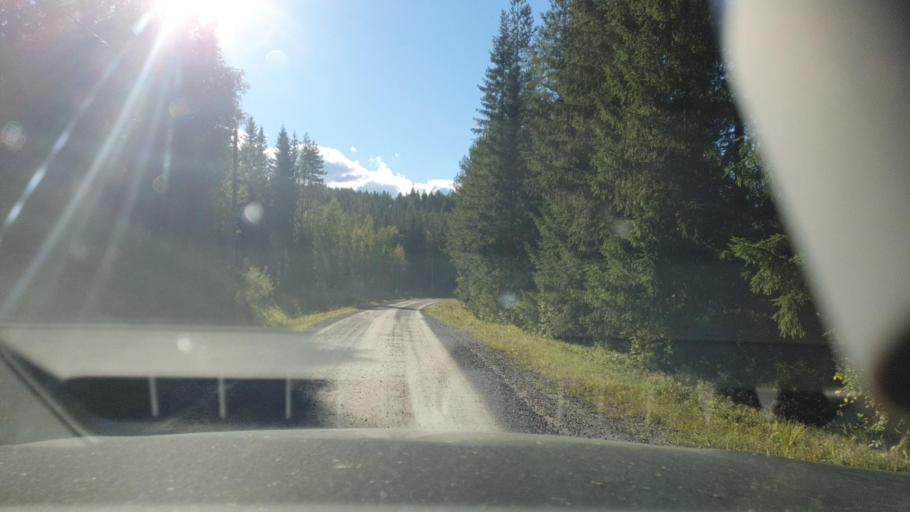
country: SE
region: Vaermland
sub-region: Filipstads Kommun
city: Filipstad
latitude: 59.8138
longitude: 13.9946
